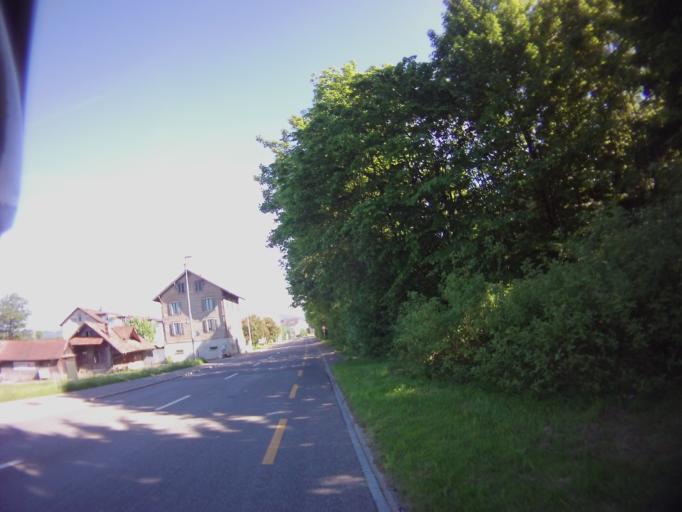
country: CH
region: Zug
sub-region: Zug
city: Cham
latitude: 47.1899
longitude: 8.4580
